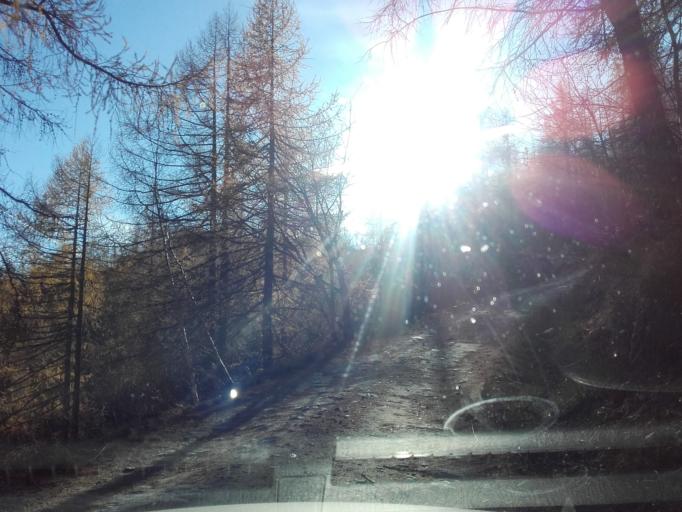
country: IT
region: Piedmont
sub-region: Provincia di Torino
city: Ribordone
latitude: 45.4354
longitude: 7.4828
